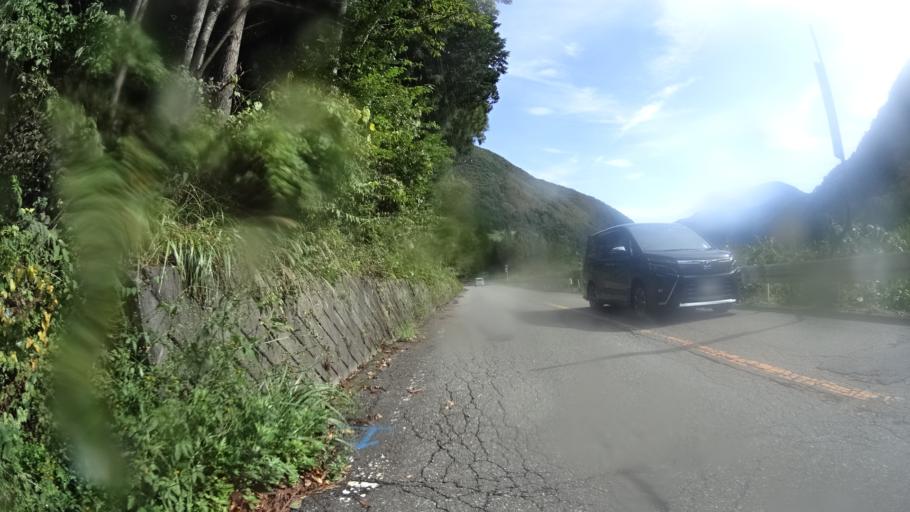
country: JP
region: Yamanashi
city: Otsuki
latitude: 35.7947
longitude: 138.9068
